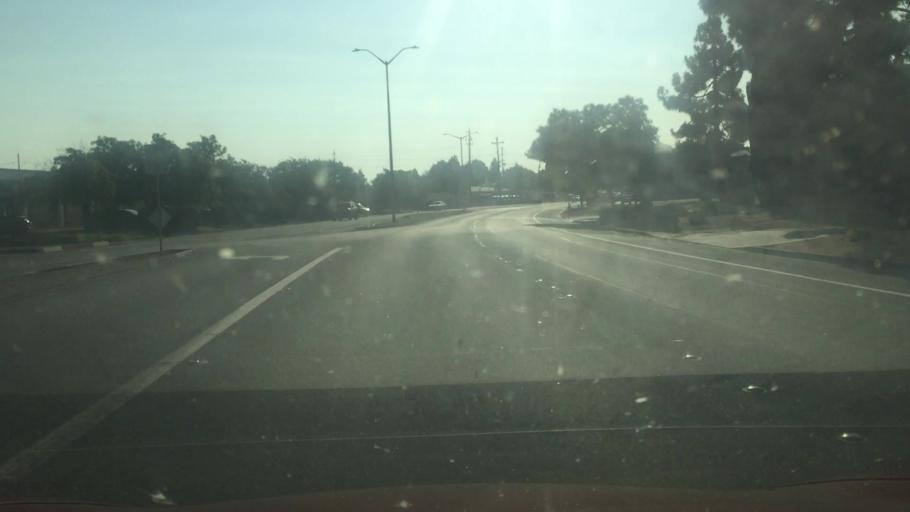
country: US
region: California
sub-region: Alameda County
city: Fremont
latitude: 37.5022
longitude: -121.9515
